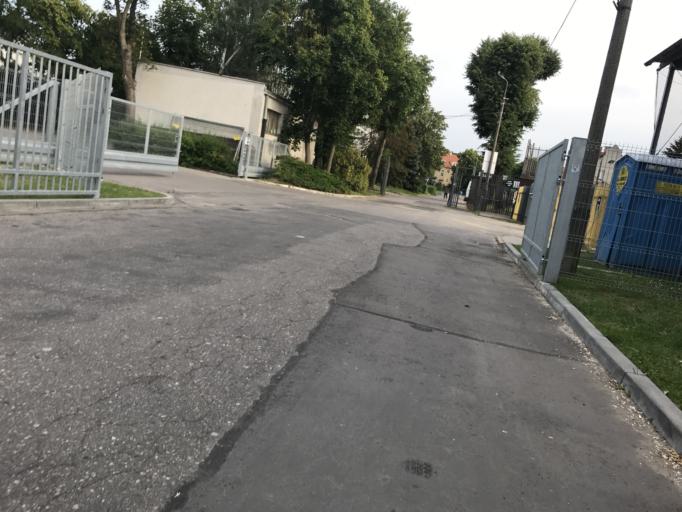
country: PL
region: Warmian-Masurian Voivodeship
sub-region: Powiat elblaski
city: Elblag
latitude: 54.1657
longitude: 19.4221
